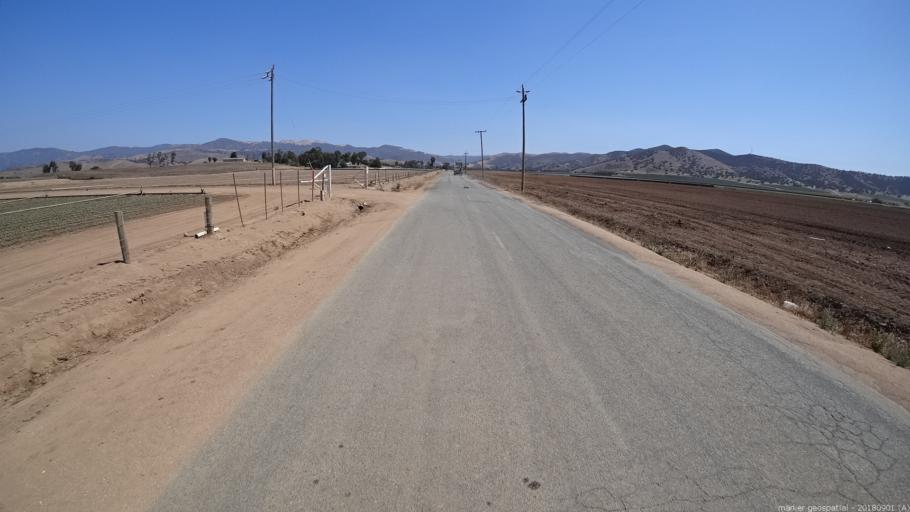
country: US
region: California
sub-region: Monterey County
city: Chualar
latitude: 36.5860
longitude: -121.4690
